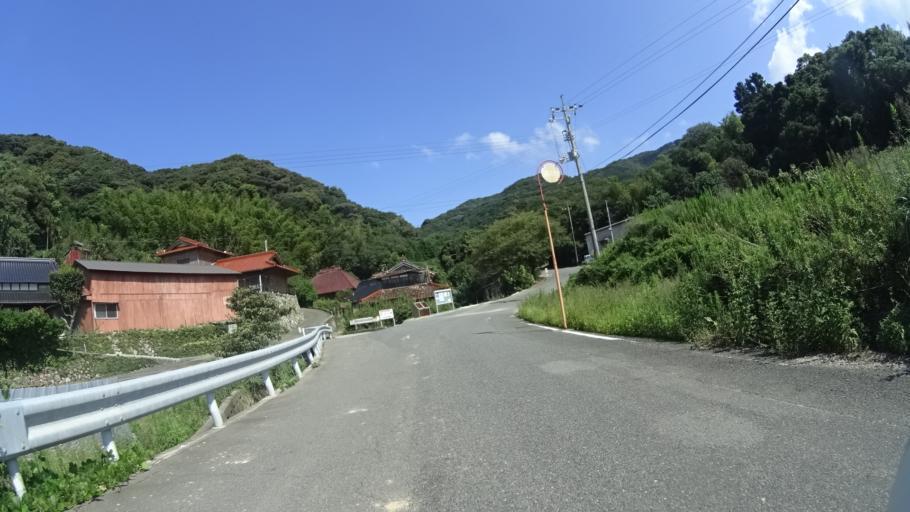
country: JP
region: Yamaguchi
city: Shimonoseki
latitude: 34.1034
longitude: 130.8684
